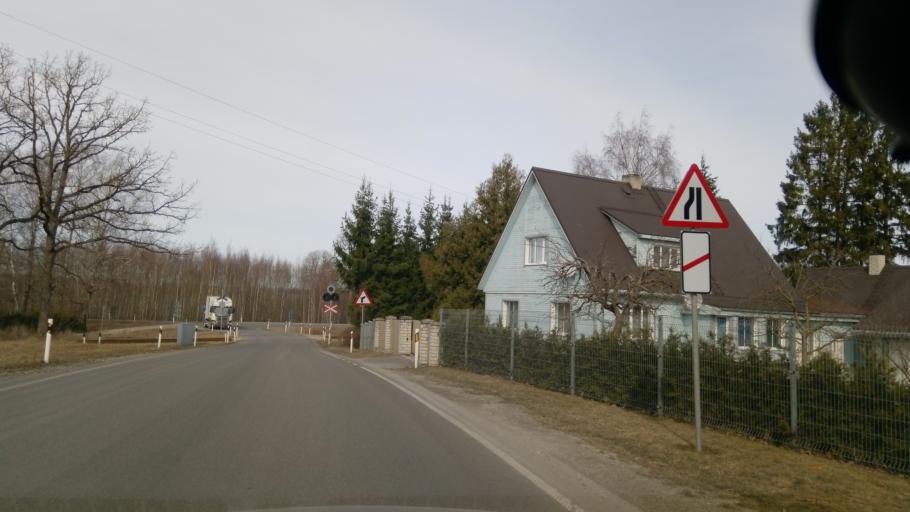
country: EE
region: Raplamaa
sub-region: Rapla vald
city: Rapla
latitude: 59.0183
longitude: 24.8380
